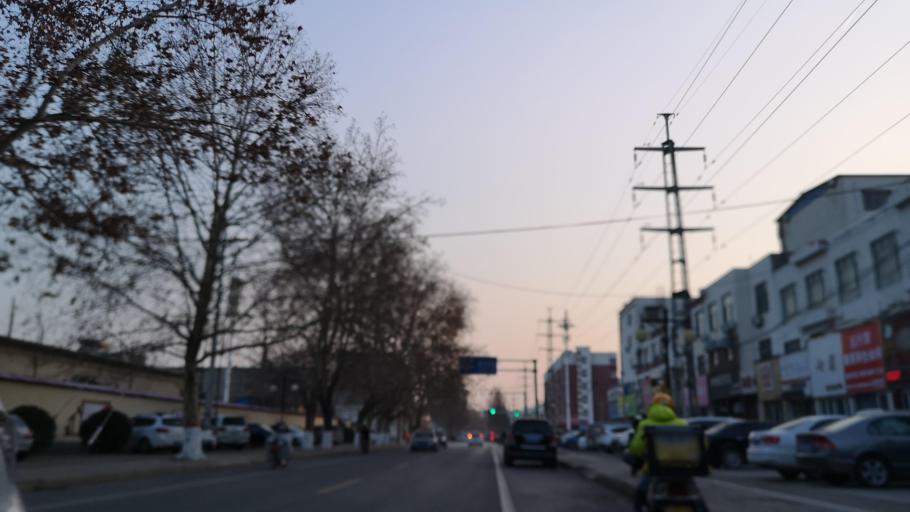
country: CN
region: Henan Sheng
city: Zhongyuanlu
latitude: 35.7694
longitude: 115.0746
